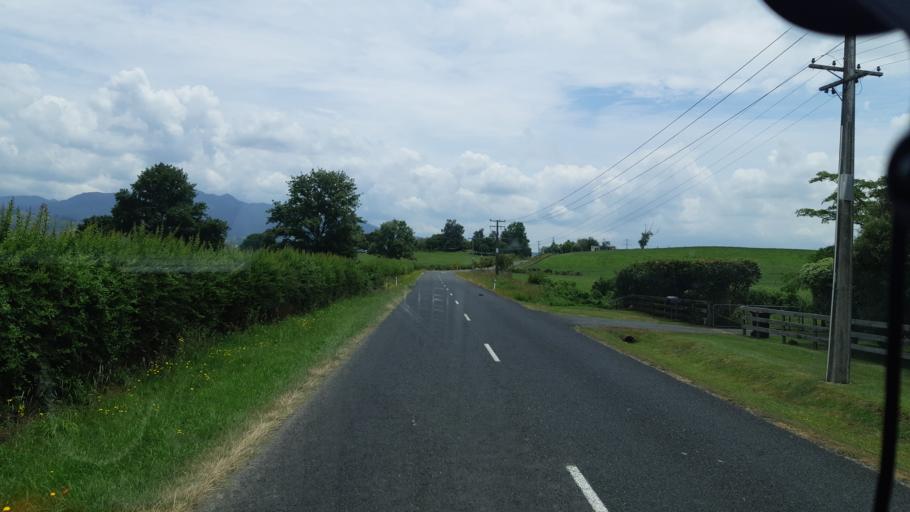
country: NZ
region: Waikato
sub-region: Otorohanga District
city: Otorohanga
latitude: -38.0038
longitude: 175.2263
